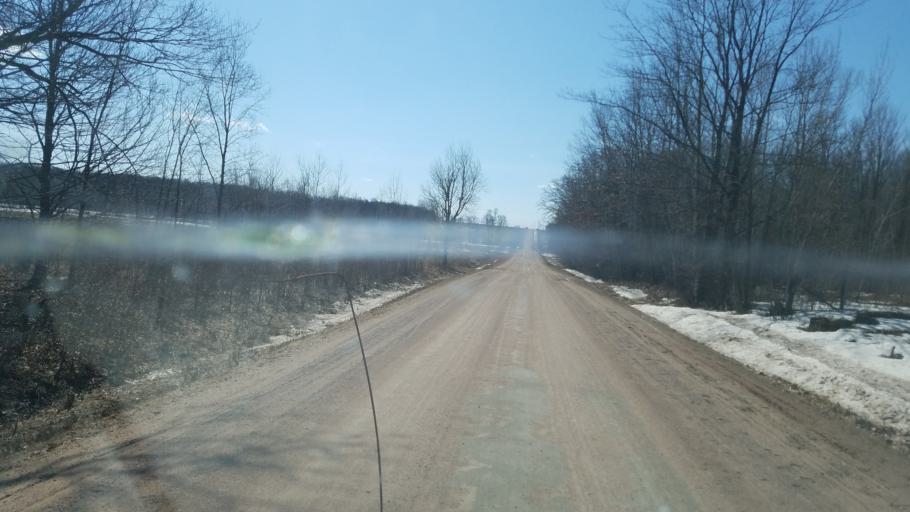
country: US
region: Wisconsin
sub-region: Clark County
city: Loyal
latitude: 44.6085
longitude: -90.3968
